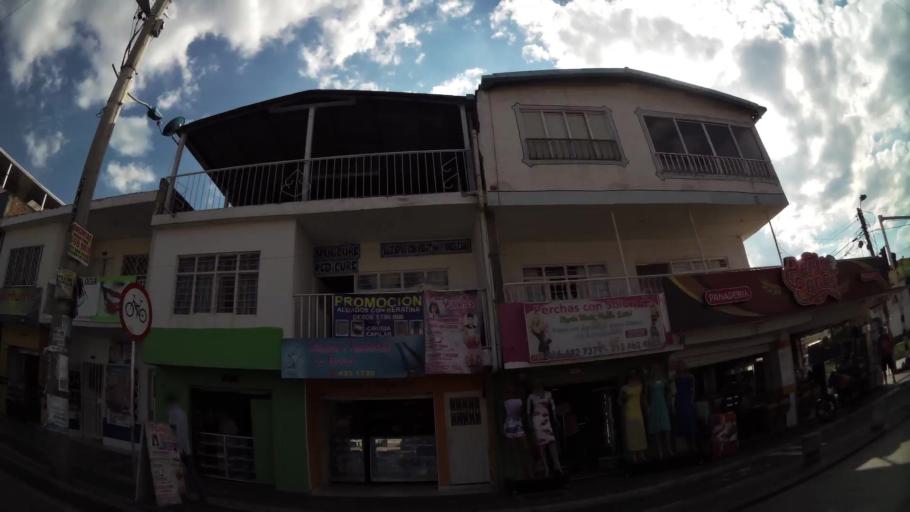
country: CO
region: Valle del Cauca
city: Cali
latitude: 3.4249
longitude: -76.4948
